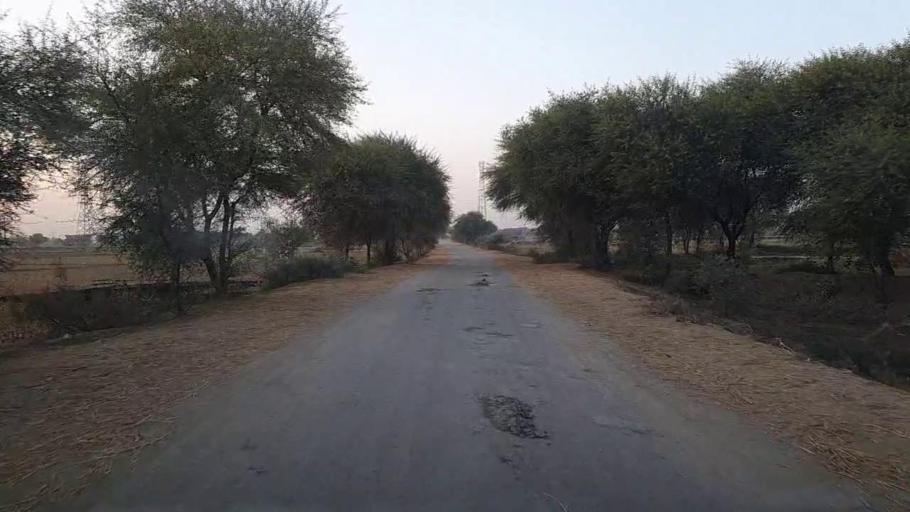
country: PK
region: Sindh
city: Kashmor
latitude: 28.4157
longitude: 69.4515
